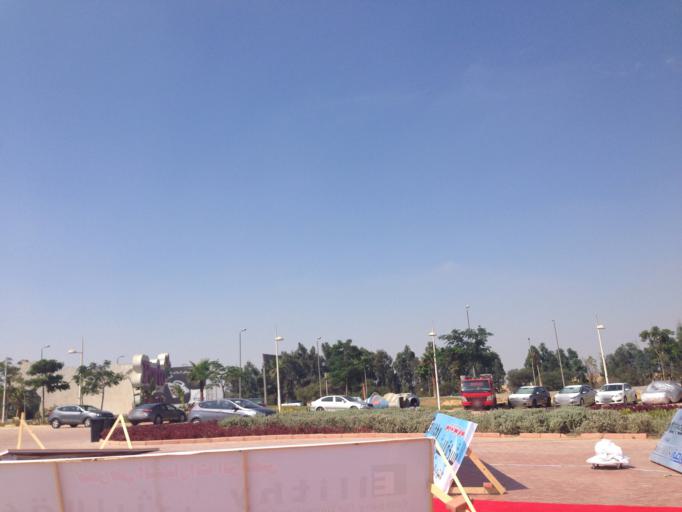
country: EG
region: Muhafazat al Qalyubiyah
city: Al Khankah
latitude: 30.0663
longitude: 31.4248
